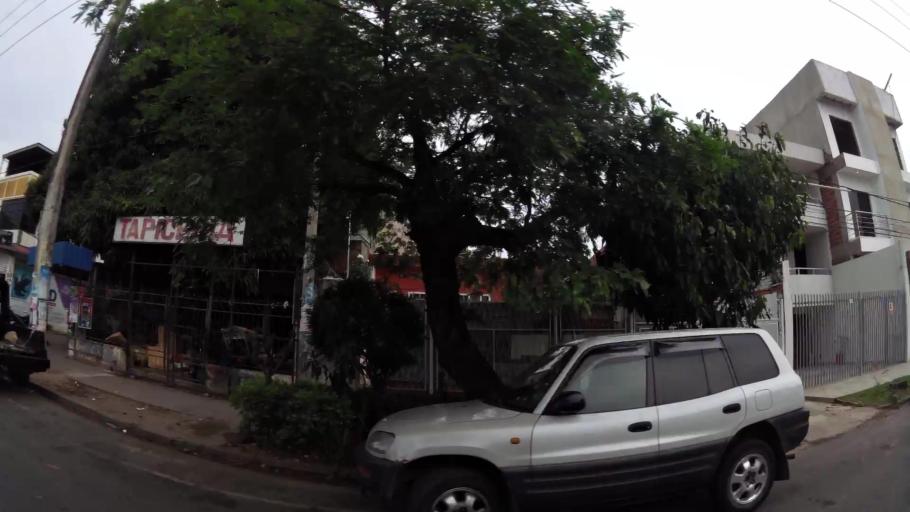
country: BO
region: Santa Cruz
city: Santa Cruz de la Sierra
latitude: -17.7848
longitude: -63.1929
